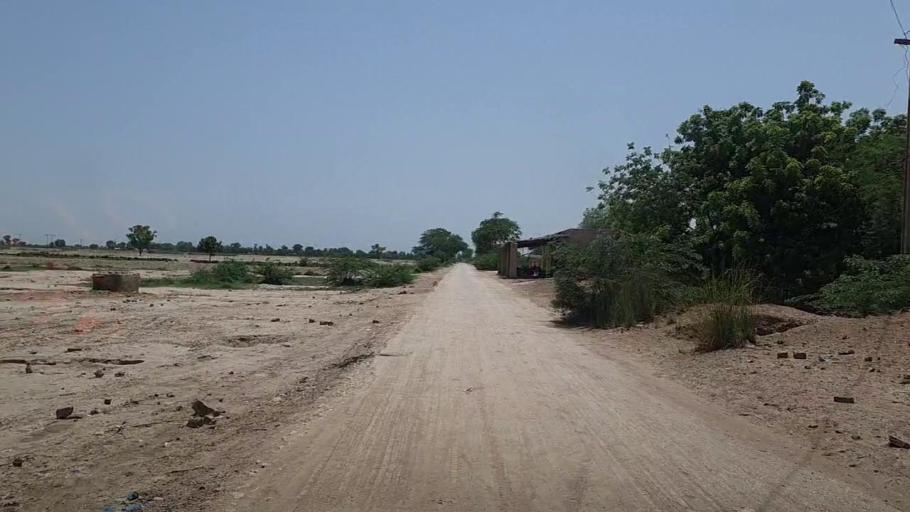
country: PK
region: Sindh
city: Pad Idan
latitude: 26.7573
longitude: 68.2936
